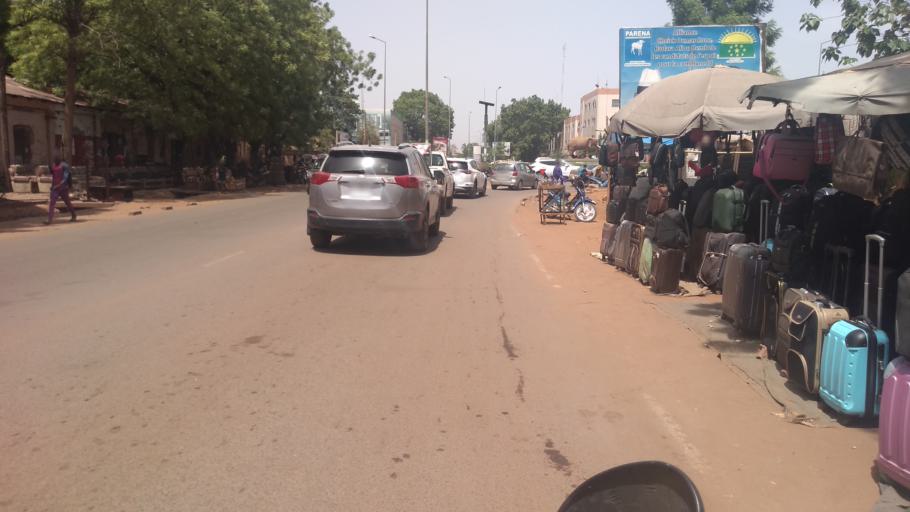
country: ML
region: Bamako
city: Bamako
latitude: 12.6422
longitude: -8.0215
